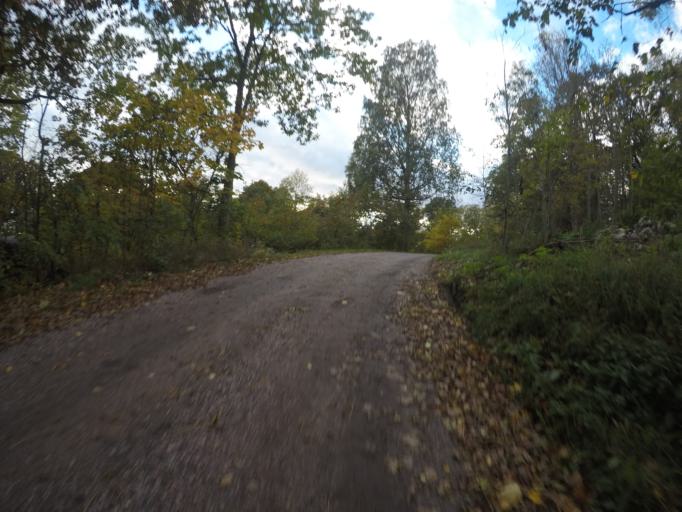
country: SE
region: Vaestmanland
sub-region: Arboga Kommun
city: Tyringe
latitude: 59.2935
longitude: 16.0049
